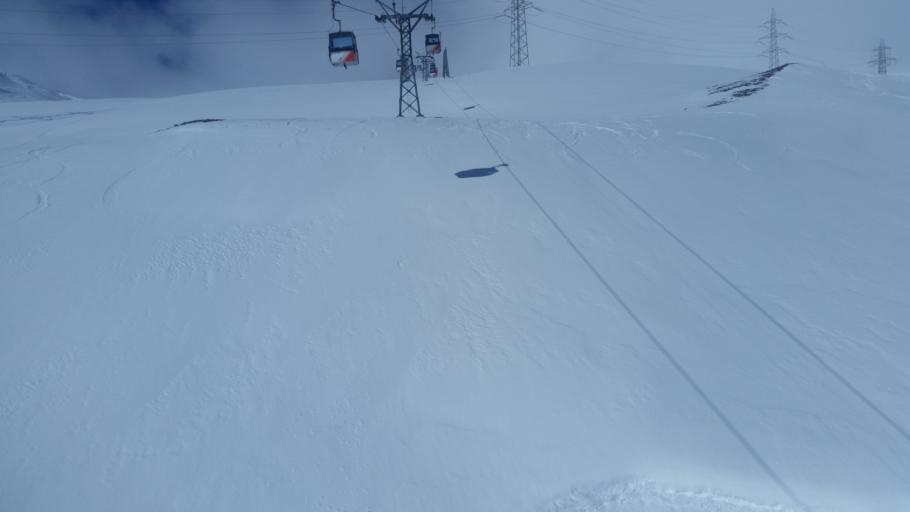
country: CH
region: Grisons
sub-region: Surselva District
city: Ilanz
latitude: 46.8649
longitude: 9.1839
